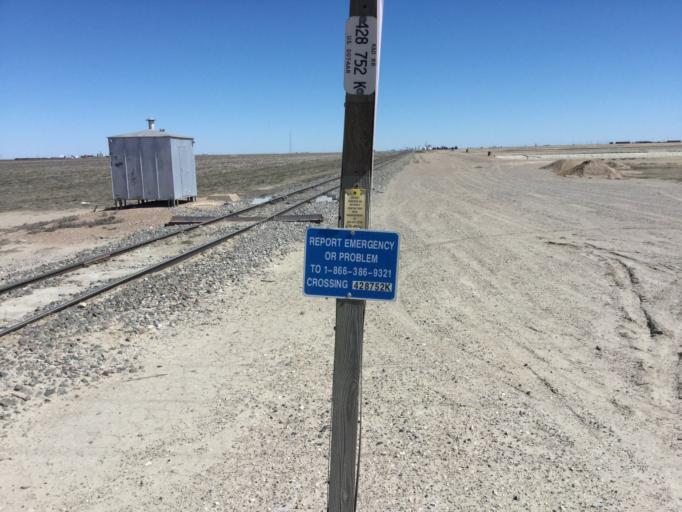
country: US
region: Kansas
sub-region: Wichita County
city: Leoti
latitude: 38.4857
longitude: -101.3309
